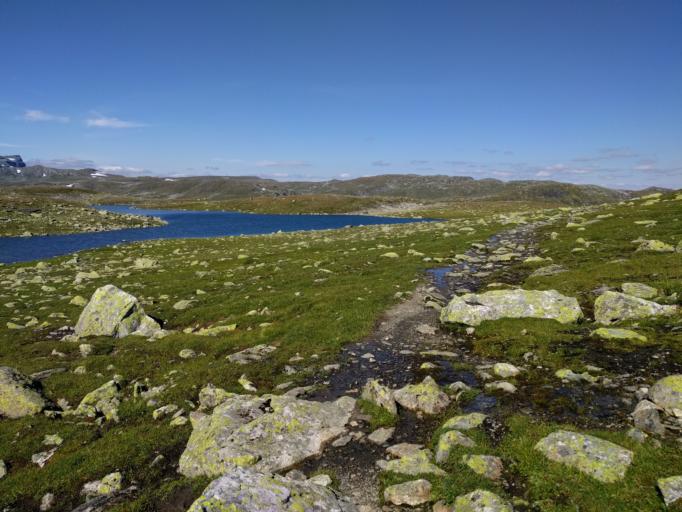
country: NO
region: Aust-Agder
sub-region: Bykle
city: Hovden
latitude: 59.8885
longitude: 7.2075
